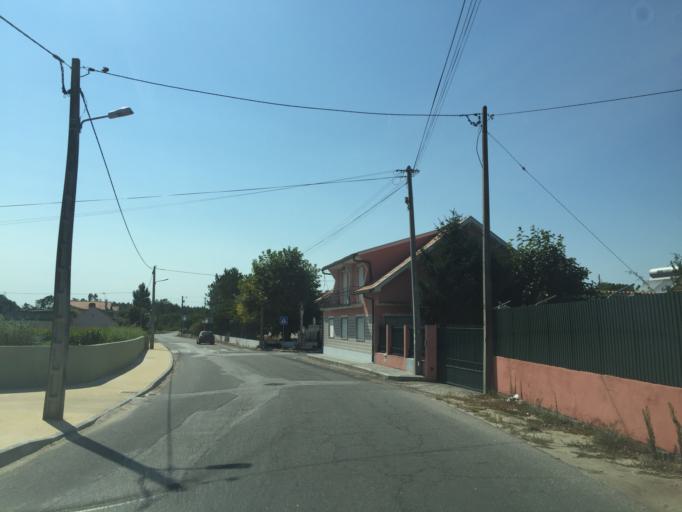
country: PT
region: Coimbra
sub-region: Montemor-O-Velho
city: Arazede
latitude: 40.3190
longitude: -8.7157
